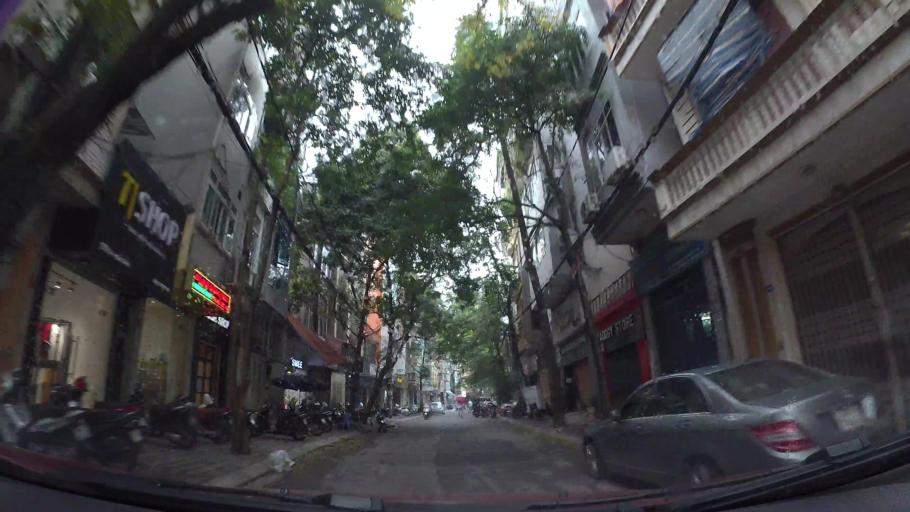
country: VN
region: Ha Noi
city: Dong Da
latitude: 21.0145
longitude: 105.8303
